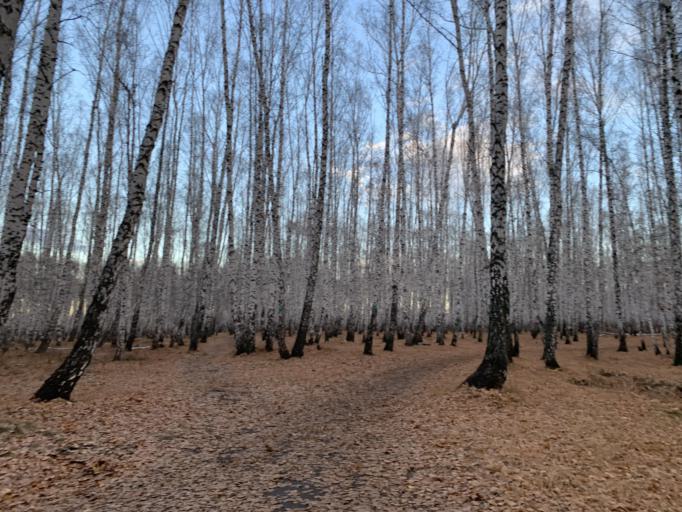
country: RU
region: Chelyabinsk
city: Roshchino
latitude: 55.2066
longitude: 61.3103
